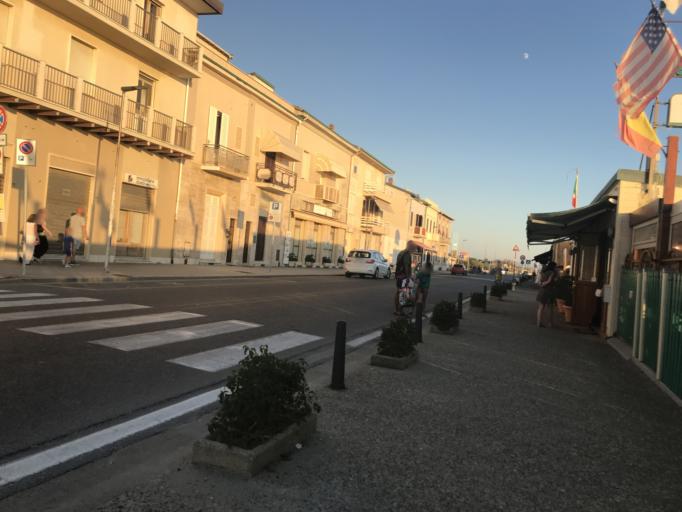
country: IT
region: Tuscany
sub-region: Province of Pisa
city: Marina di Pisa
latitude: 43.6599
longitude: 10.2795
